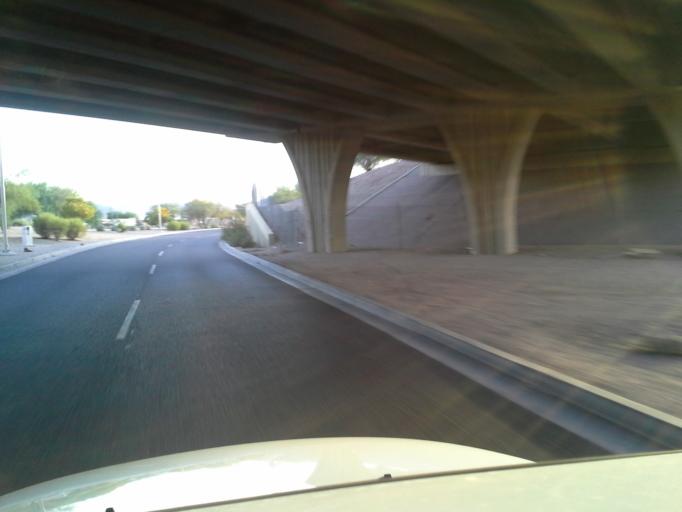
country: US
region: Arizona
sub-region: Maricopa County
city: Phoenix
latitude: 33.4378
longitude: -112.0301
